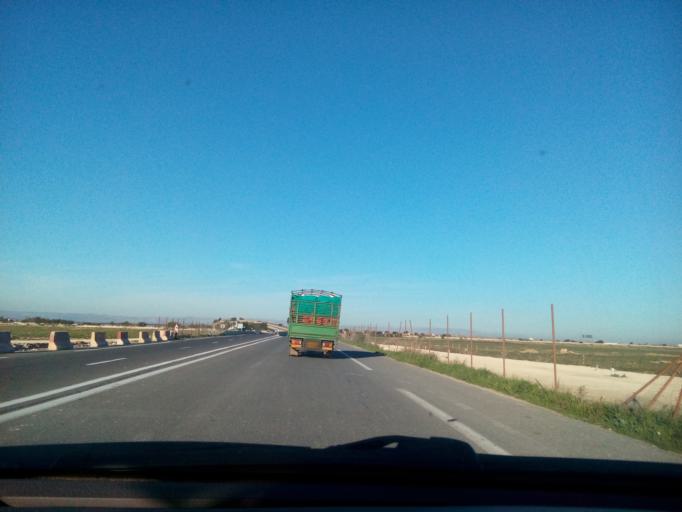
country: DZ
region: Relizane
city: Relizane
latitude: 35.7925
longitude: 0.5353
